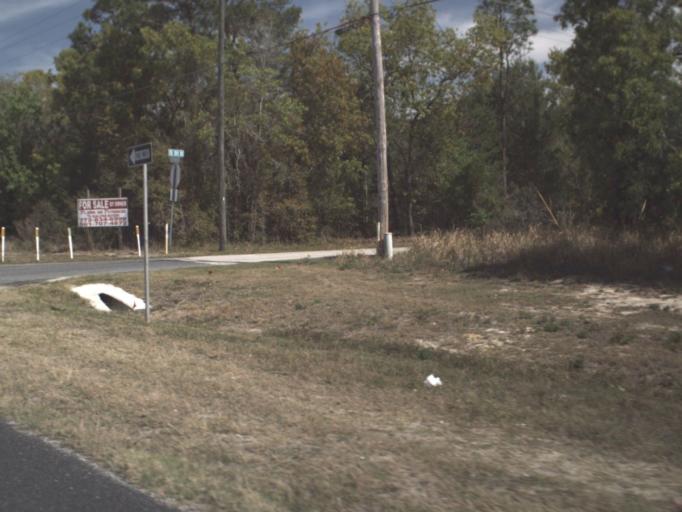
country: US
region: Florida
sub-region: Sumter County
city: The Villages
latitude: 28.9959
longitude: -81.9974
